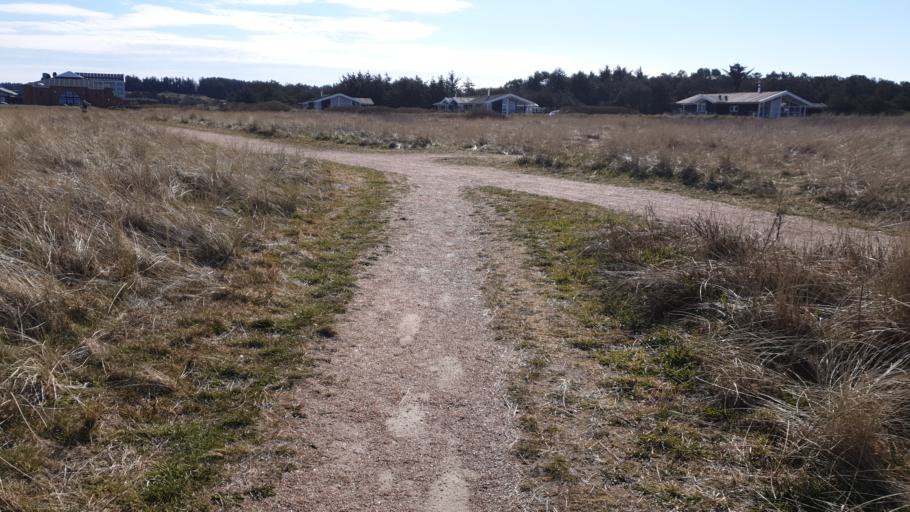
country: DK
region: North Denmark
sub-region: Hjorring Kommune
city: Hjorring
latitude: 57.4932
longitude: 9.8330
